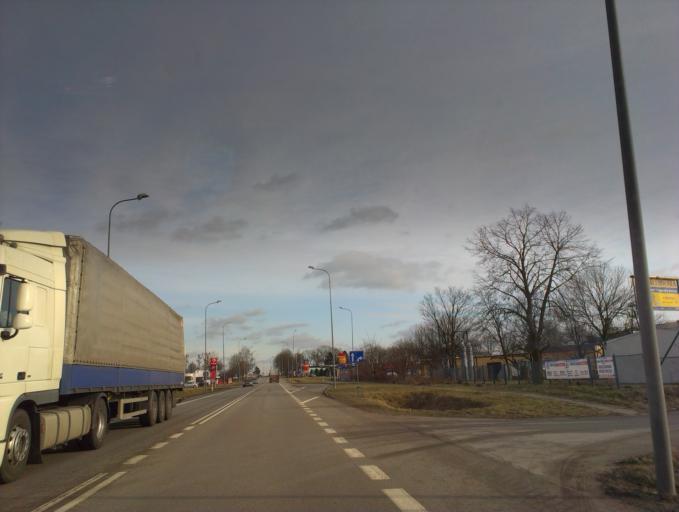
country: PL
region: Kujawsko-Pomorskie
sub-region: Powiat lipnowski
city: Lipno
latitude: 52.8512
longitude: 19.1974
